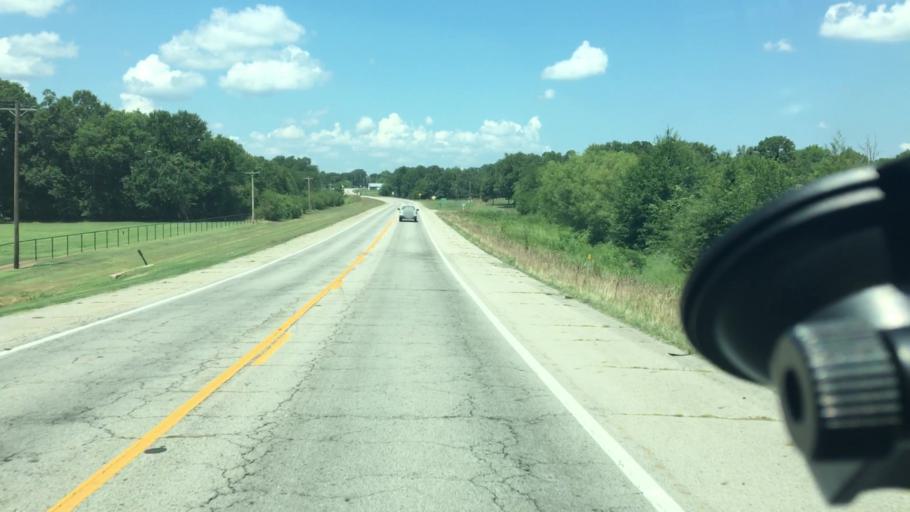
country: US
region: Arkansas
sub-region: Sebastian County
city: Lavaca
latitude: 35.2922
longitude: -94.1270
